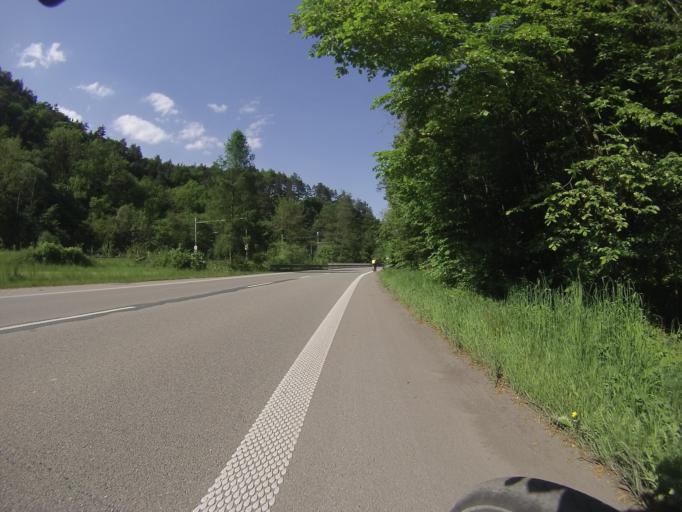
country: CZ
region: South Moravian
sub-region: Okres Blansko
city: Blansko
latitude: 49.3387
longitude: 16.6487
